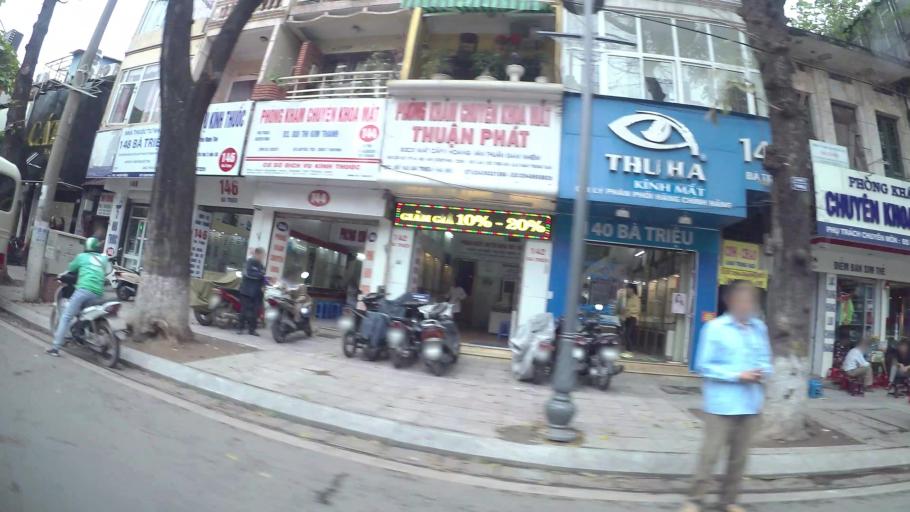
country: VN
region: Ha Noi
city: Hai BaTrung
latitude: 21.0176
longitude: 105.8493
